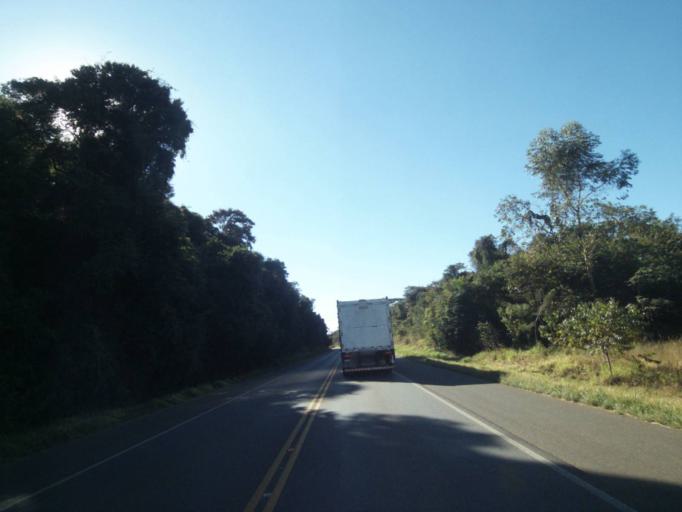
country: BR
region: Parana
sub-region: Tibagi
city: Tibagi
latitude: -24.5616
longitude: -50.4547
